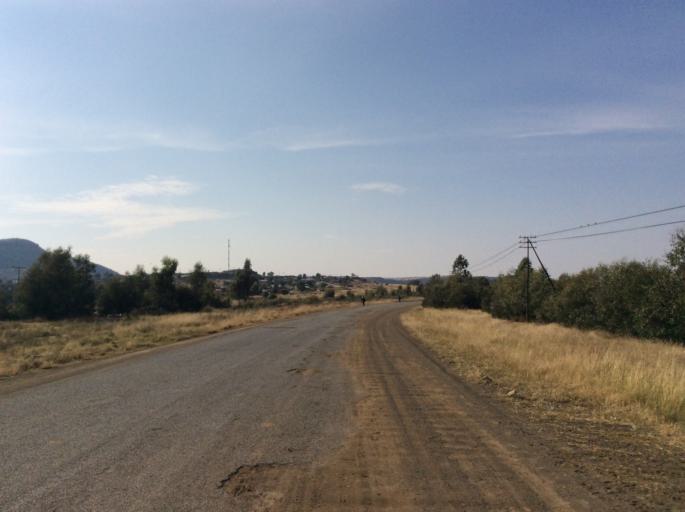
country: LS
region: Mafeteng
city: Mafeteng
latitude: -29.7224
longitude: 27.0204
